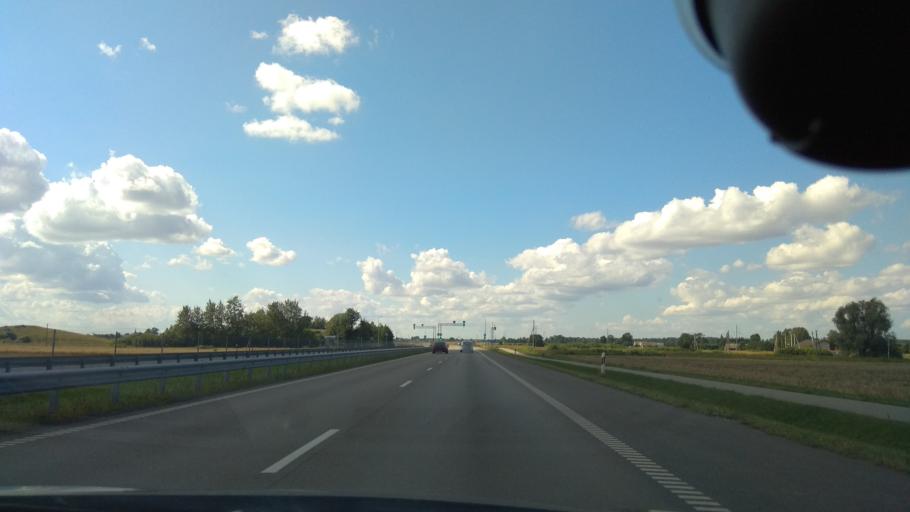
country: LT
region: Siauliu apskritis
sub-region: Siauliai
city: Siauliai
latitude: 55.9686
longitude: 23.1900
